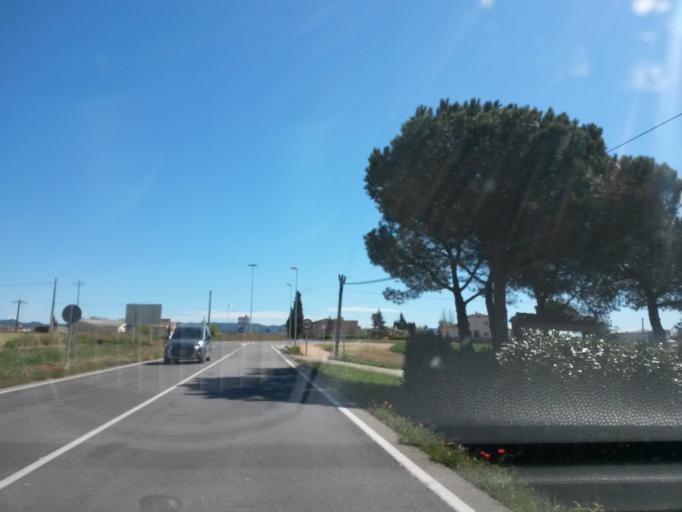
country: ES
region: Catalonia
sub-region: Provincia de Girona
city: Riudellots de la Selva
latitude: 41.8924
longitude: 2.7944
